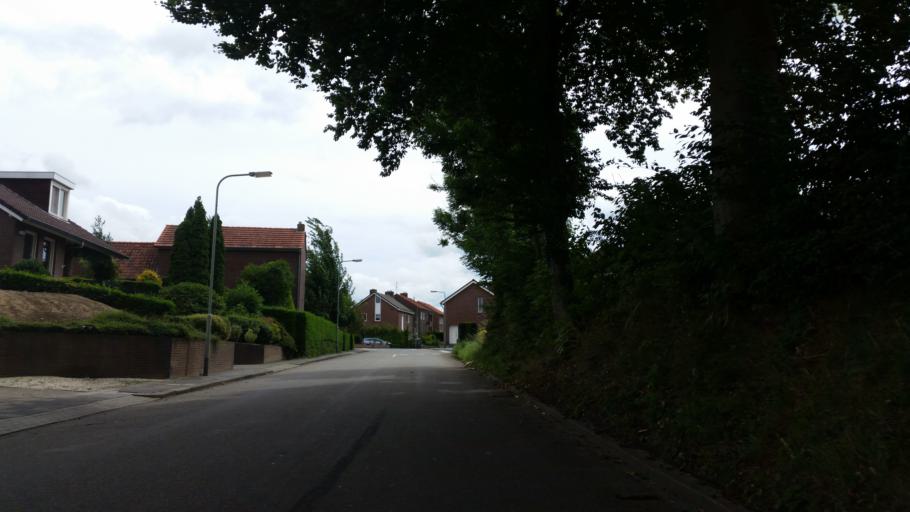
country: NL
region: Limburg
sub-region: Eijsden-Margraten
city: Margraten
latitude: 50.8212
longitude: 5.8169
